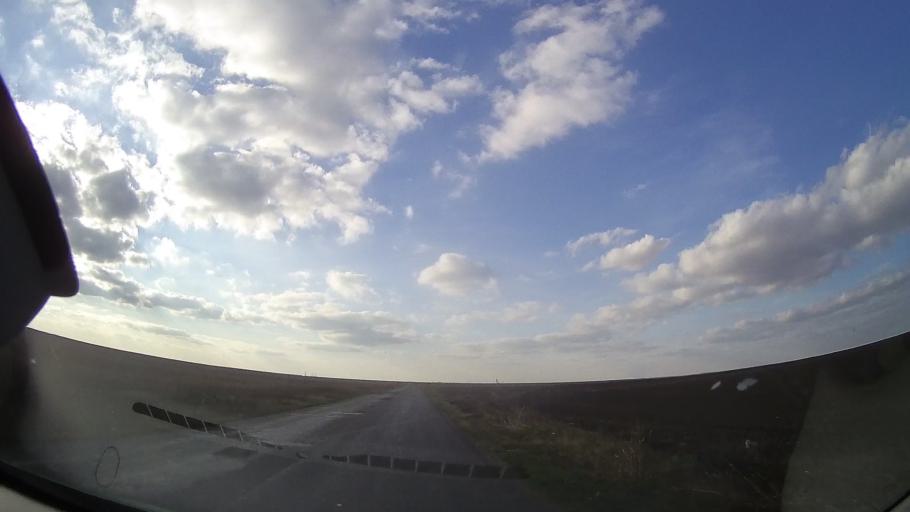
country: RO
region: Constanta
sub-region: Comuna Negru Voda
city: Negru Voda
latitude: 43.8208
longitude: 28.1697
